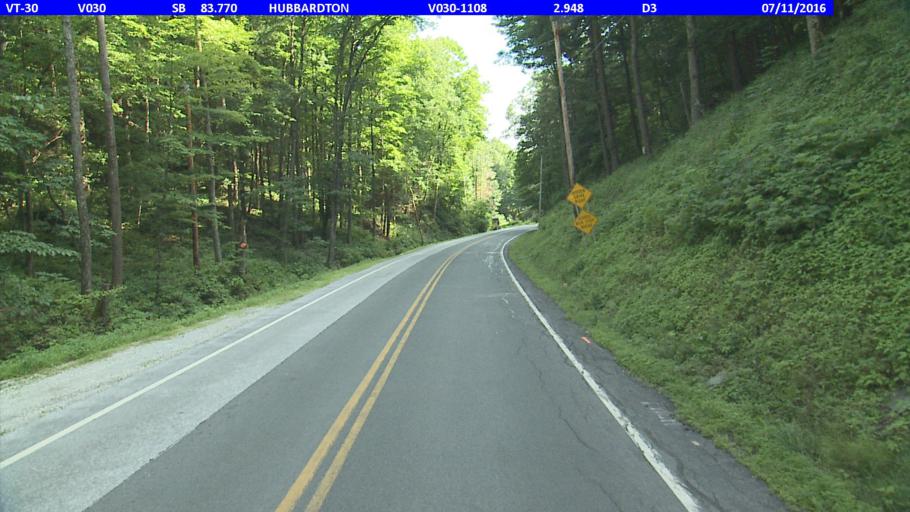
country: US
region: Vermont
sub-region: Rutland County
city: Castleton
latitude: 43.7204
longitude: -73.1847
